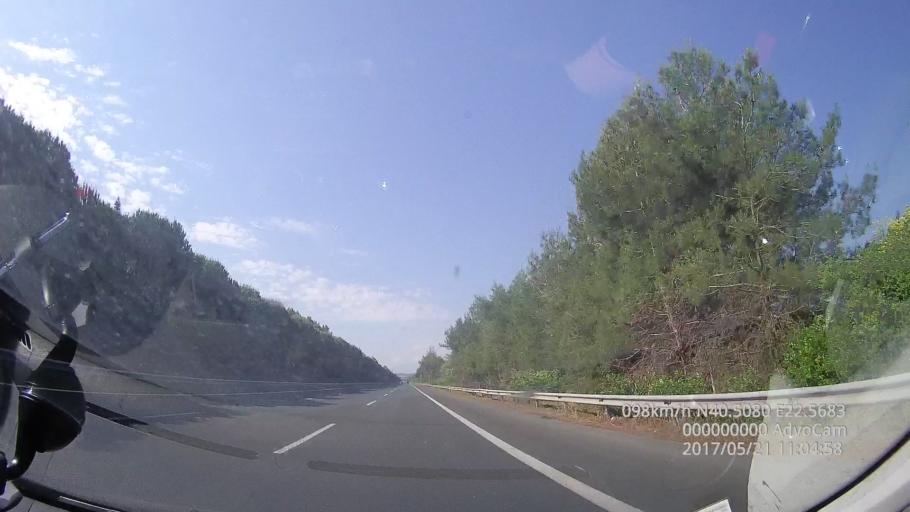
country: GR
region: Central Macedonia
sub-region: Nomos Pierias
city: Aiginio
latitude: 40.5073
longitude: 22.5681
